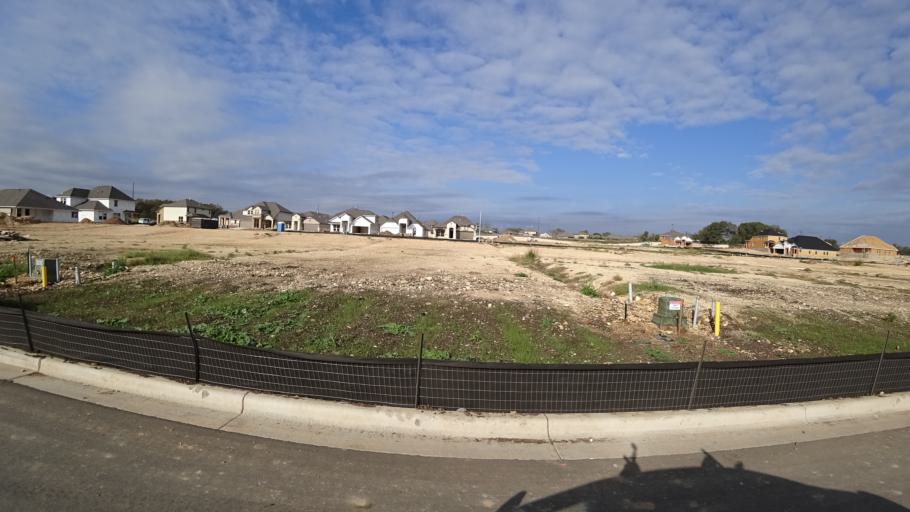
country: US
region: Texas
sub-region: Travis County
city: Manchaca
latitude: 30.1295
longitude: -97.8443
